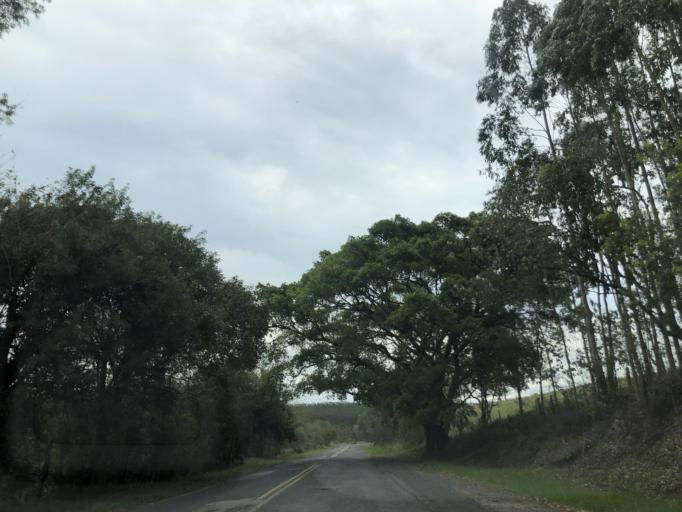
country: BR
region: Sao Paulo
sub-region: Pilar Do Sul
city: Pilar do Sul
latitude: -23.8146
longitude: -47.6341
